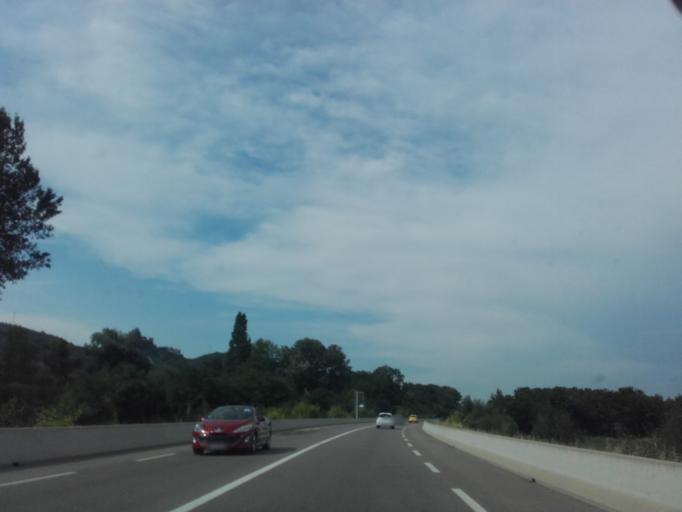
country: FR
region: Rhone-Alpes
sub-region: Departement de l'Ardeche
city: Rochemaure
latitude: 44.5751
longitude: 4.6991
